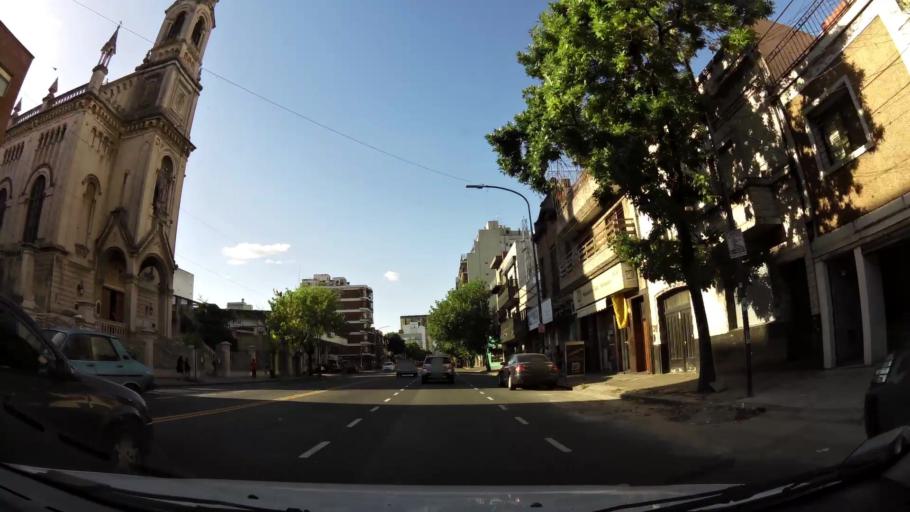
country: AR
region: Buenos Aires F.D.
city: Buenos Aires
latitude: -34.6266
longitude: -58.4267
